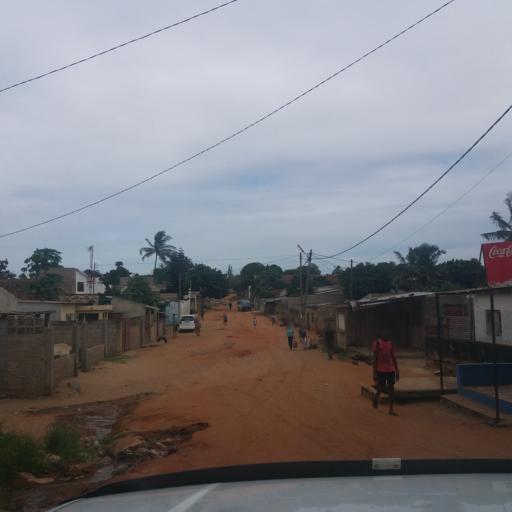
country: MZ
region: Maputo City
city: Maputo
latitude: -25.9134
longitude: 32.5937
